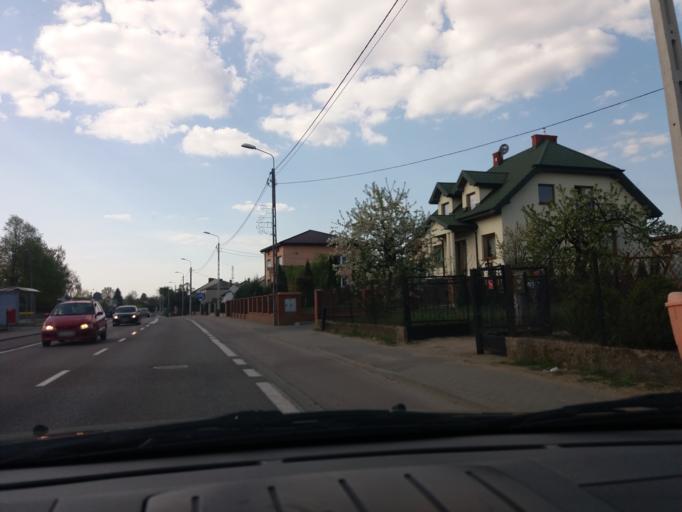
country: PL
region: Masovian Voivodeship
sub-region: Powiat mlawski
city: Mlawa
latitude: 53.1275
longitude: 20.3566
